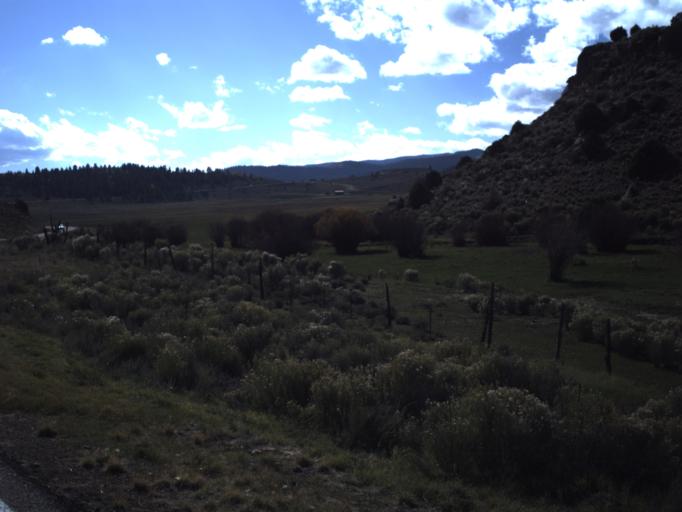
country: US
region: Utah
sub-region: Garfield County
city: Panguitch
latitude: 37.7298
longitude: -112.6064
